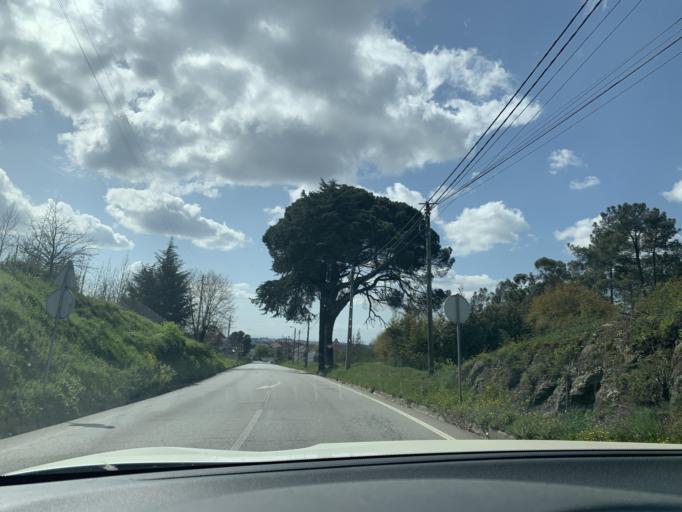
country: PT
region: Viseu
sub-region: Viseu
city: Rio de Loba
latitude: 40.6950
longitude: -7.8735
